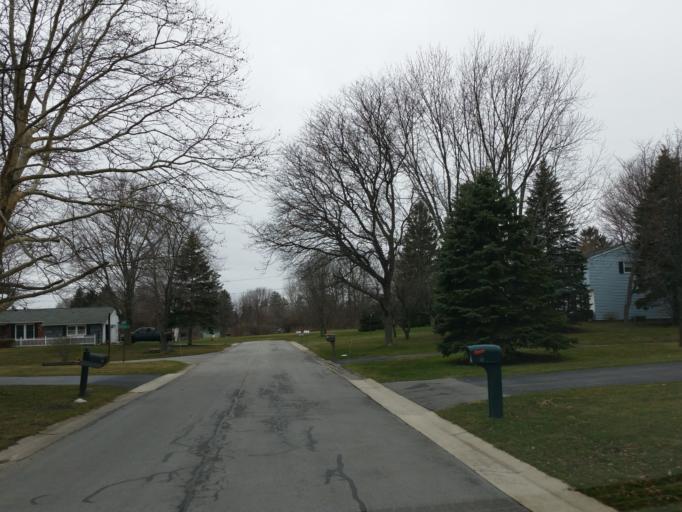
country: US
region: New York
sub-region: Monroe County
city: Scottsville
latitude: 43.1107
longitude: -77.7604
